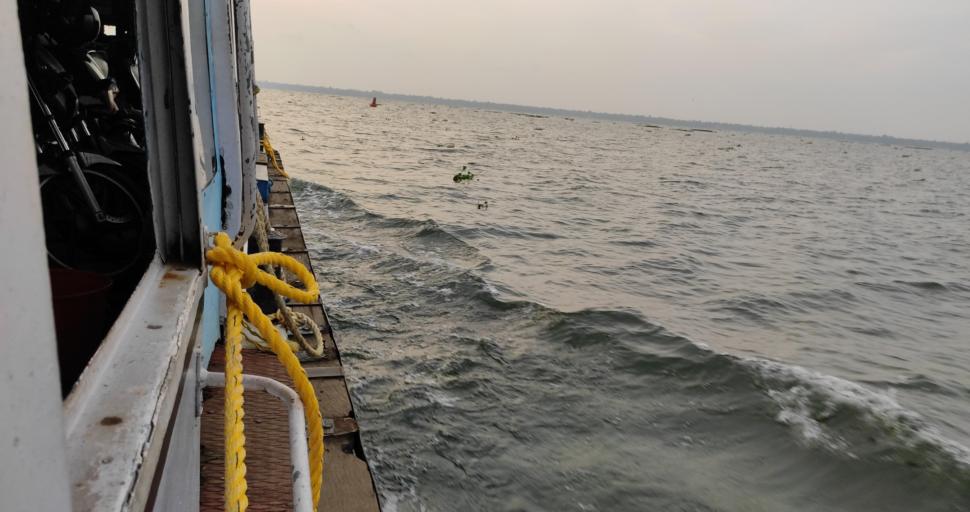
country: IN
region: Kerala
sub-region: Alappuzha
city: Shertallai
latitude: 9.6031
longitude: 76.3893
